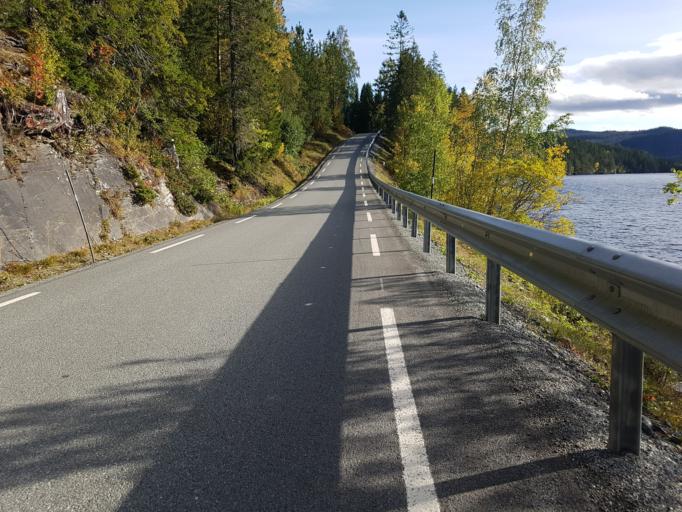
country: NO
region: Sor-Trondelag
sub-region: Malvik
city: Malvik
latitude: 63.3589
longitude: 10.6340
